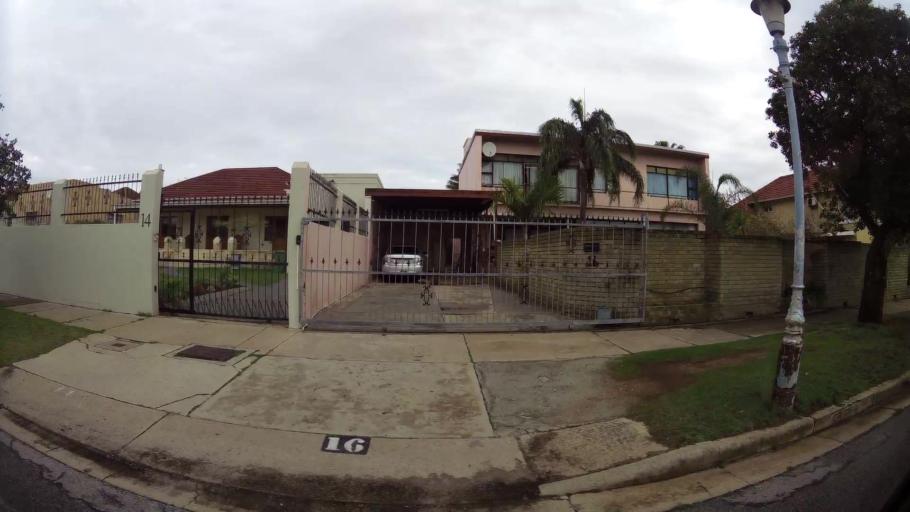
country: ZA
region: Eastern Cape
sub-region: Nelson Mandela Bay Metropolitan Municipality
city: Port Elizabeth
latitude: -33.9541
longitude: 25.6004
